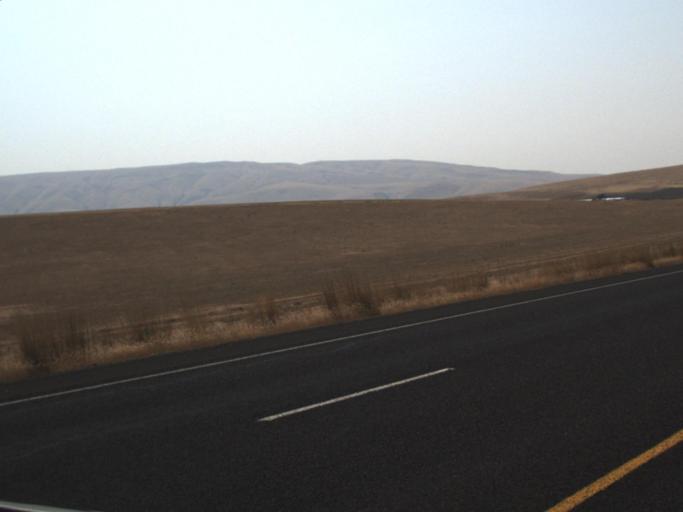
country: US
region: Washington
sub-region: Grant County
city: Desert Aire
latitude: 46.5433
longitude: -119.8443
